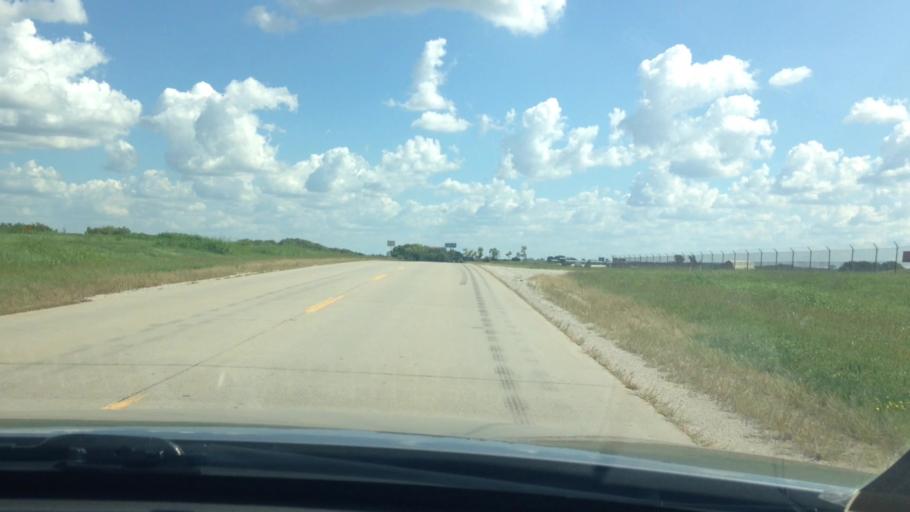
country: US
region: Missouri
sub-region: Platte County
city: Platte City
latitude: 39.3300
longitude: -94.7179
